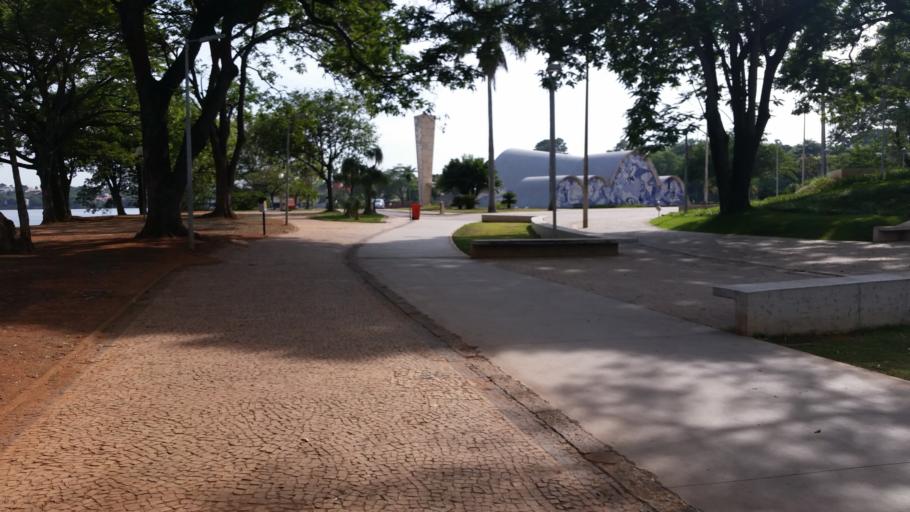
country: BR
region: Minas Gerais
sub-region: Belo Horizonte
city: Belo Horizonte
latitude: -19.8589
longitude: -43.9799
